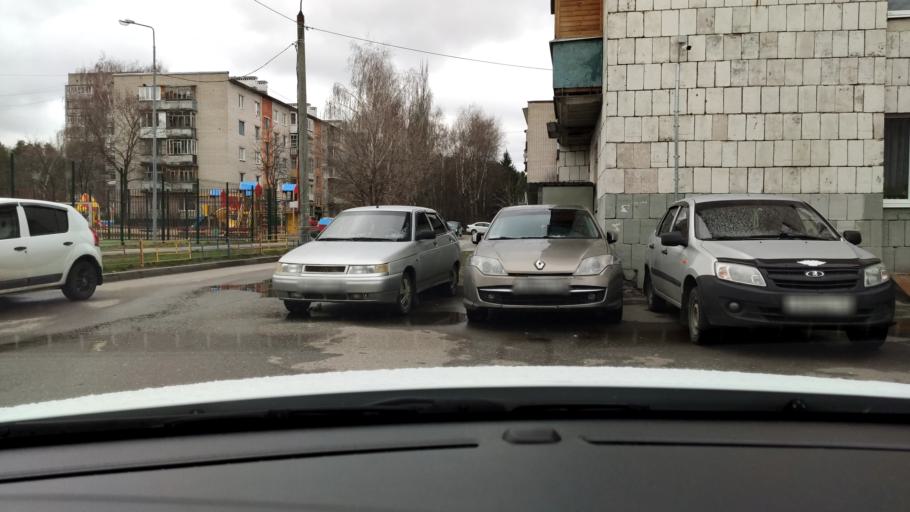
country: RU
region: Tatarstan
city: Vysokaya Gora
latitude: 55.8600
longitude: 49.2283
